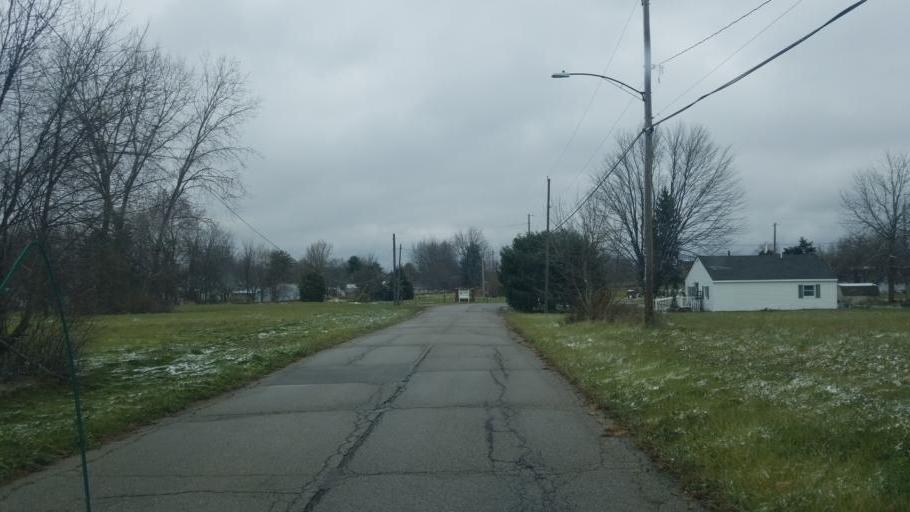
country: US
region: Ohio
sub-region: Richland County
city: Shelby
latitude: 40.8939
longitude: -82.6543
